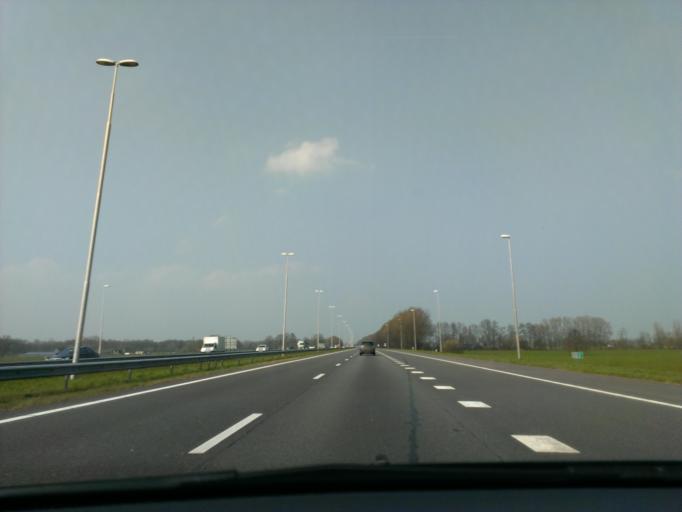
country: NL
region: Gelderland
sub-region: Gemeente Epe
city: Emst
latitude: 52.2969
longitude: 6.0093
